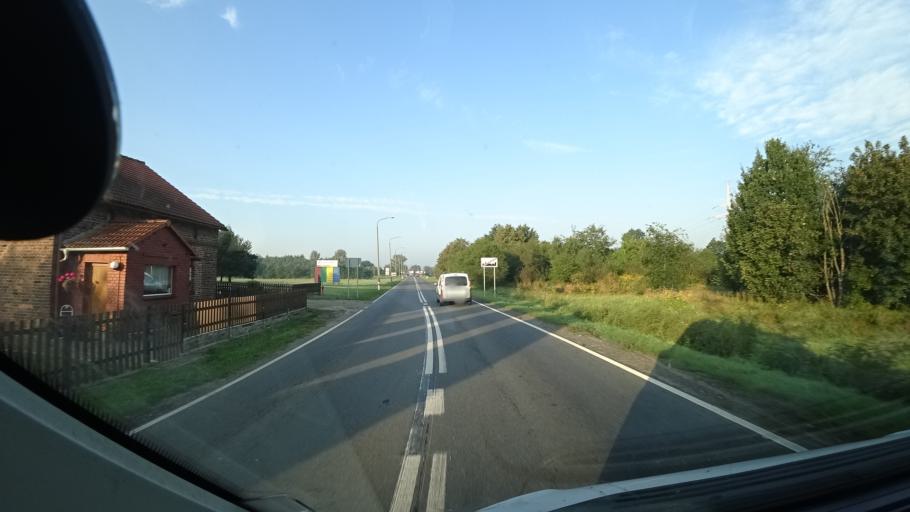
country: PL
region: Opole Voivodeship
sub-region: Powiat kedzierzynsko-kozielski
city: Slawiecice
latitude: 50.3646
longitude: 18.2755
